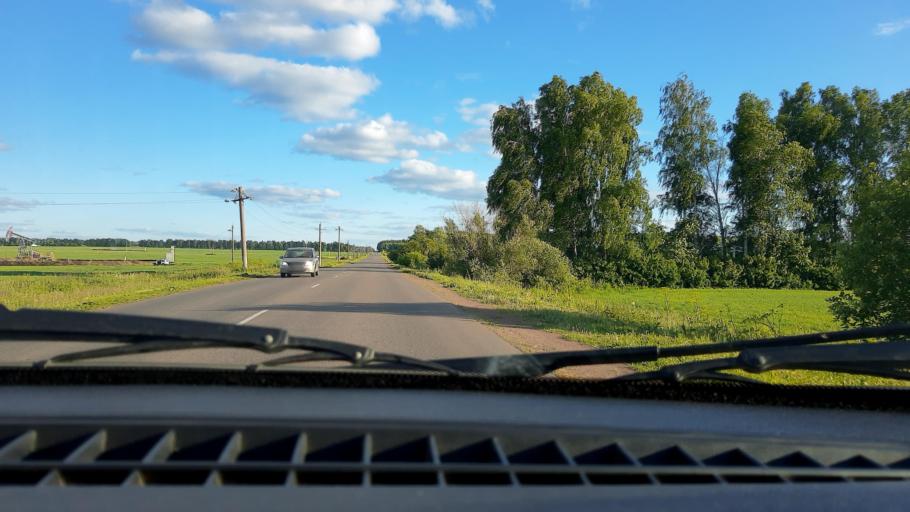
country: RU
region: Bashkortostan
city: Mikhaylovka
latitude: 54.8758
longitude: 55.8567
